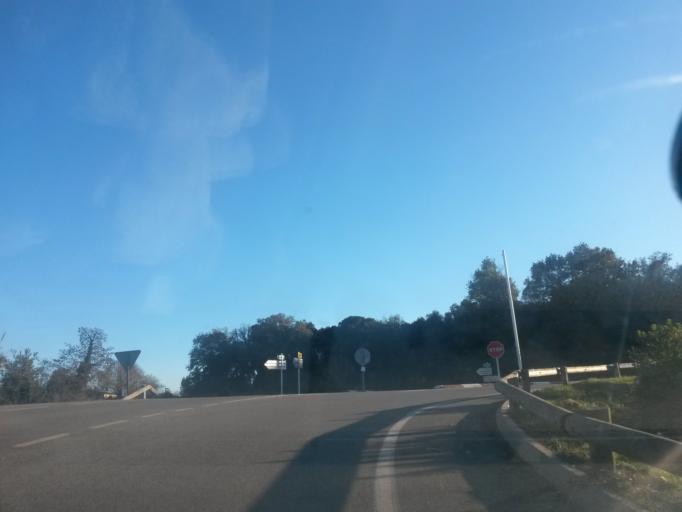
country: ES
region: Catalonia
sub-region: Provincia de Girona
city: Aiguaviva
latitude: 41.9323
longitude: 2.7421
